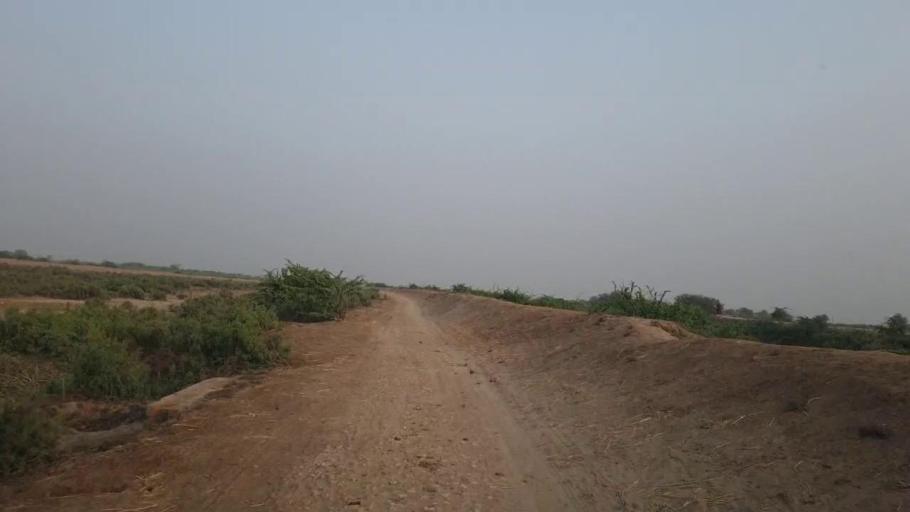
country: PK
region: Sindh
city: Mirpur Batoro
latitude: 24.6431
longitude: 68.3756
